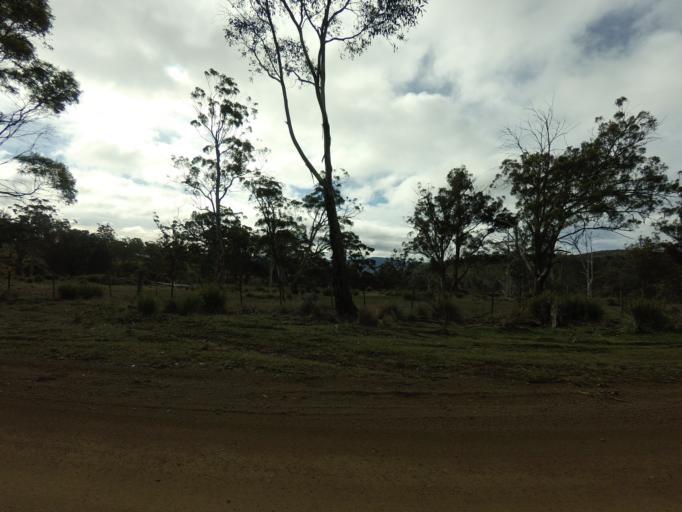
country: AU
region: Tasmania
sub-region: Derwent Valley
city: New Norfolk
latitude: -42.7362
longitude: 146.8688
